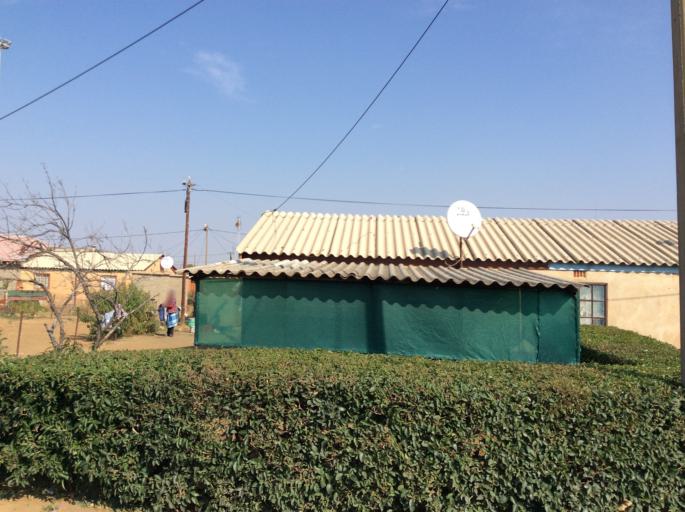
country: LS
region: Mafeteng
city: Mafeteng
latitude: -29.7171
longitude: 27.0294
